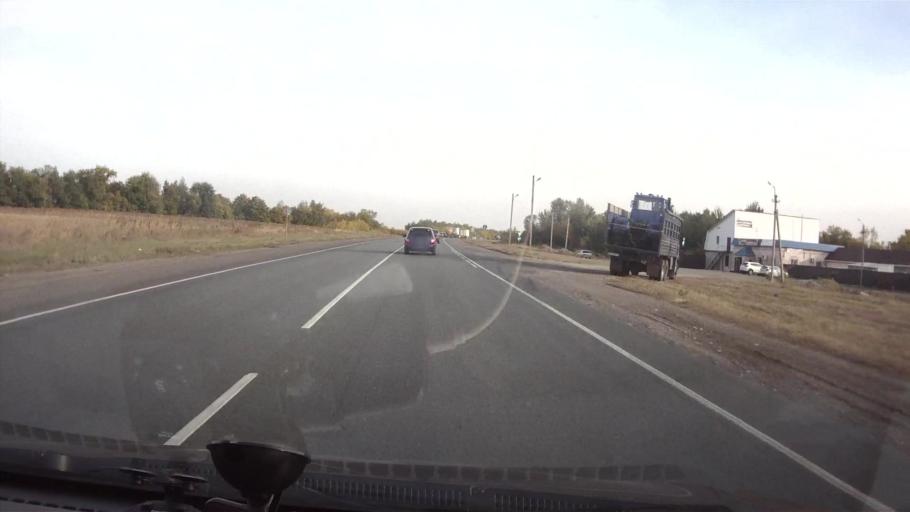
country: RU
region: Saratov
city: Sokolovyy
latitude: 51.5344
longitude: 45.8001
